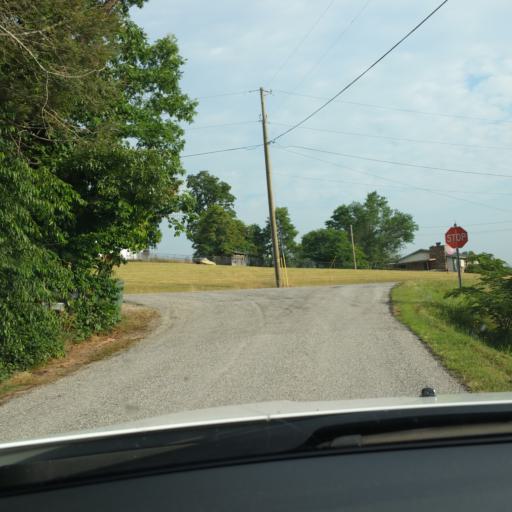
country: US
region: North Carolina
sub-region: Buncombe County
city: Bent Creek
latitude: 35.5131
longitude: -82.6896
